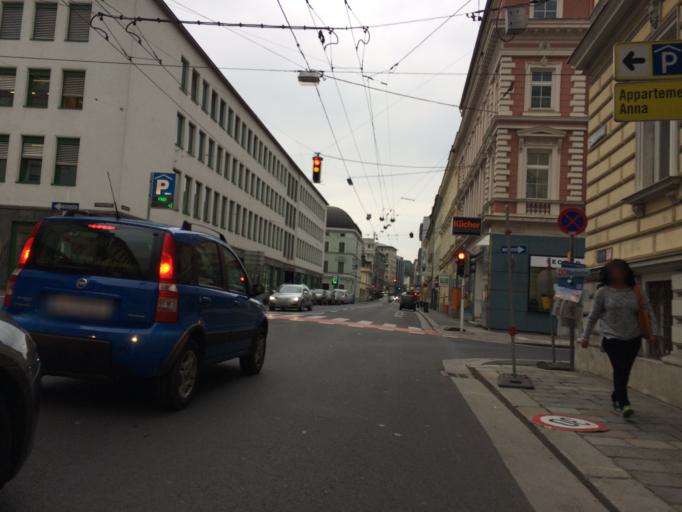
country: AT
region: Upper Austria
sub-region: Linz Stadt
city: Linz
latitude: 48.3020
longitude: 14.2947
